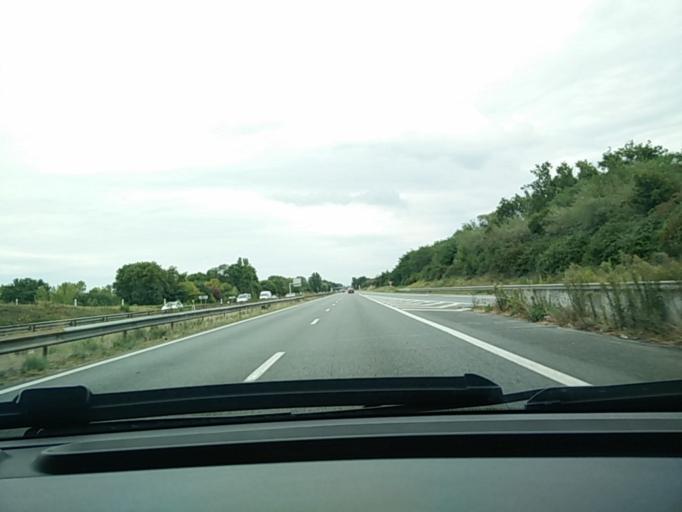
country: FR
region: Aquitaine
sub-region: Departement de la Gironde
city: Eysines
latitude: 44.8659
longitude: -0.6515
